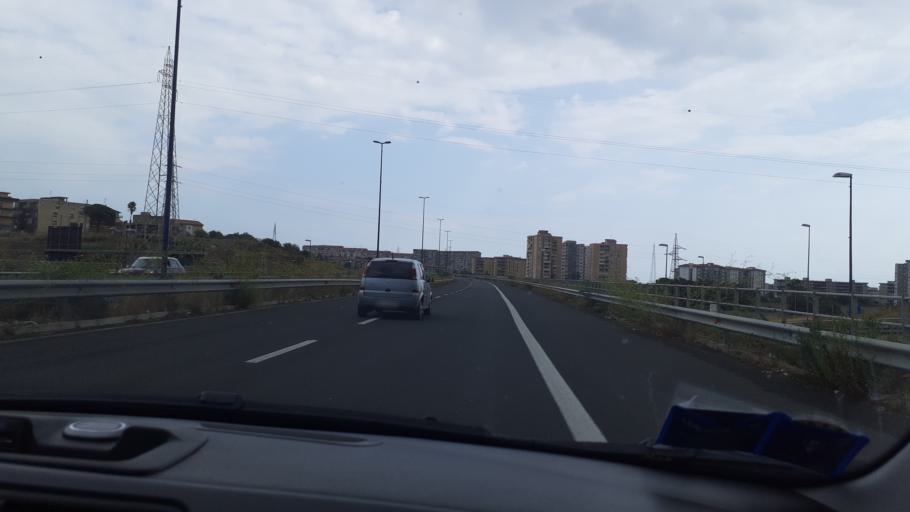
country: IT
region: Sicily
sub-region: Catania
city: Catania
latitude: 37.4819
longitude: 15.0513
